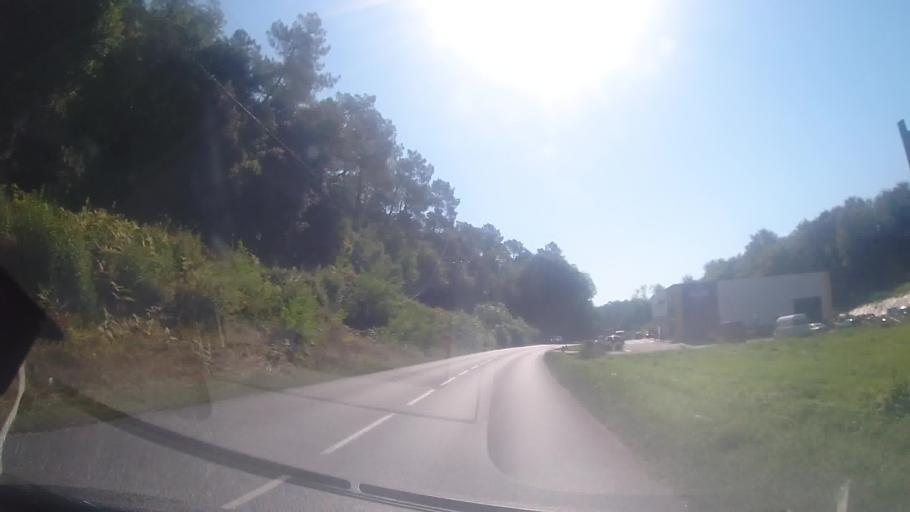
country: FR
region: Aquitaine
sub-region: Departement de la Dordogne
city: Sarlat-la-Caneda
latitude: 44.8723
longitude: 1.2407
